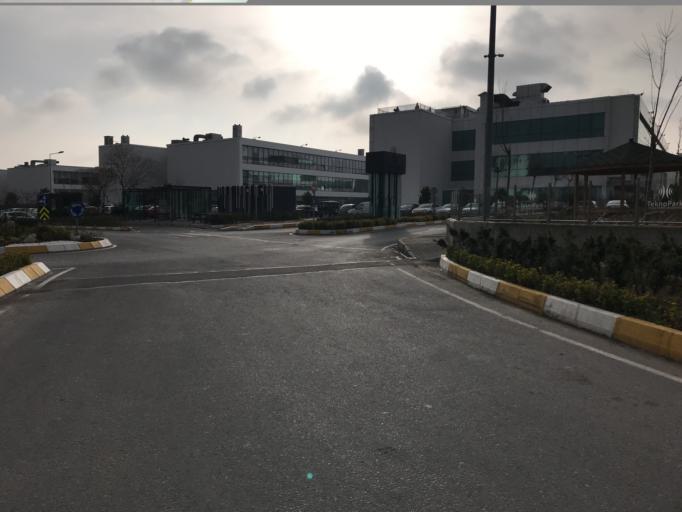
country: TR
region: Istanbul
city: merter keresteciler
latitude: 41.0211
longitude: 28.8885
